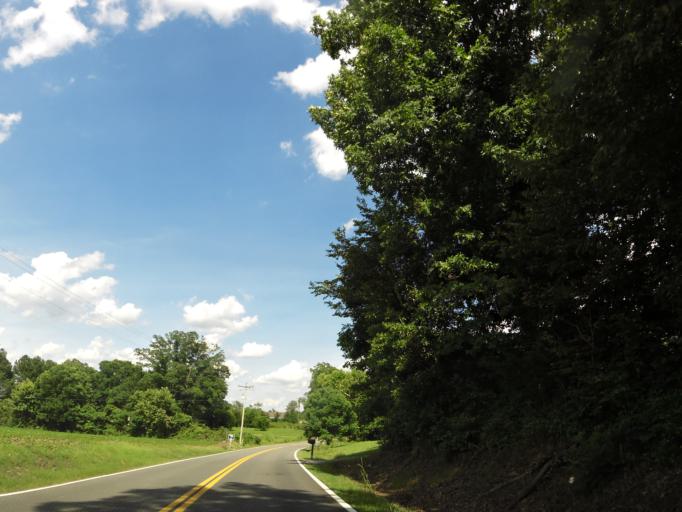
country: US
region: Tennessee
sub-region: Gibson County
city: Milan
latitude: 35.9775
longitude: -88.8014
